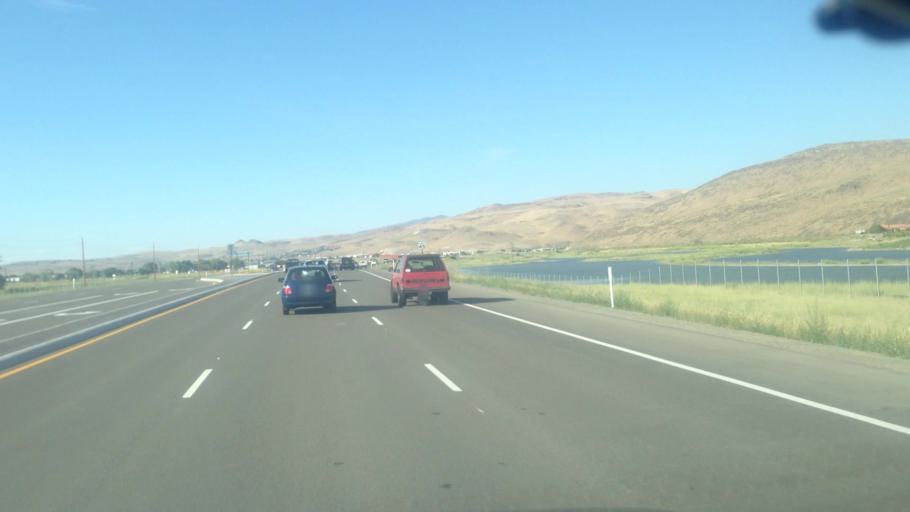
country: US
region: Nevada
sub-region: Washoe County
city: Sparks
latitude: 39.4990
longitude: -119.7287
